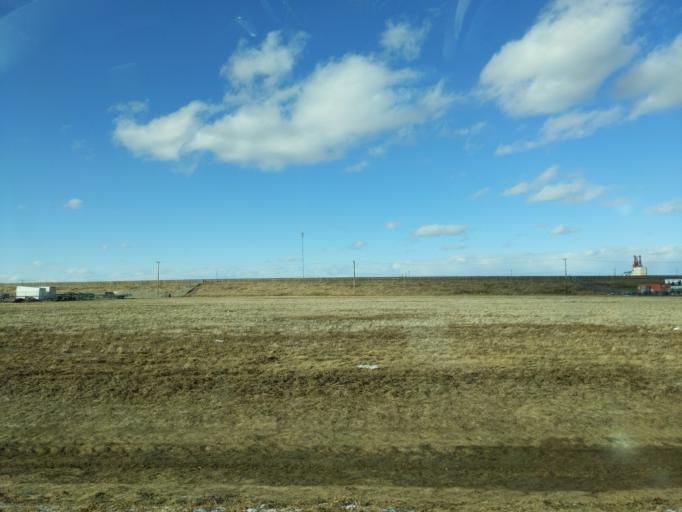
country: CA
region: Saskatchewan
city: Lloydminster
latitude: 53.2439
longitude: -109.9759
